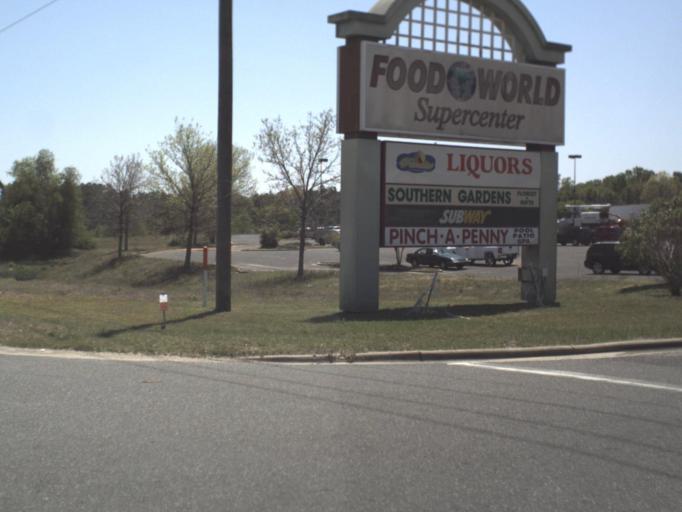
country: US
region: Florida
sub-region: Escambia County
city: Ensley
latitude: 30.5160
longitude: -87.3118
